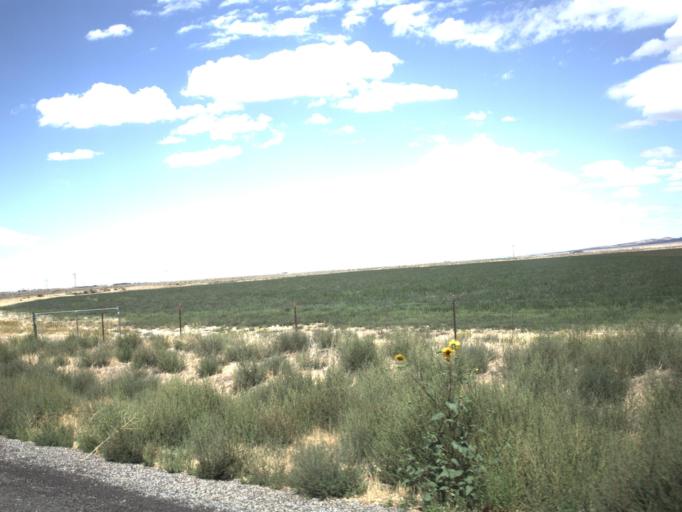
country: US
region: Utah
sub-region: Millard County
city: Fillmore
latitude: 39.1415
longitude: -112.3772
